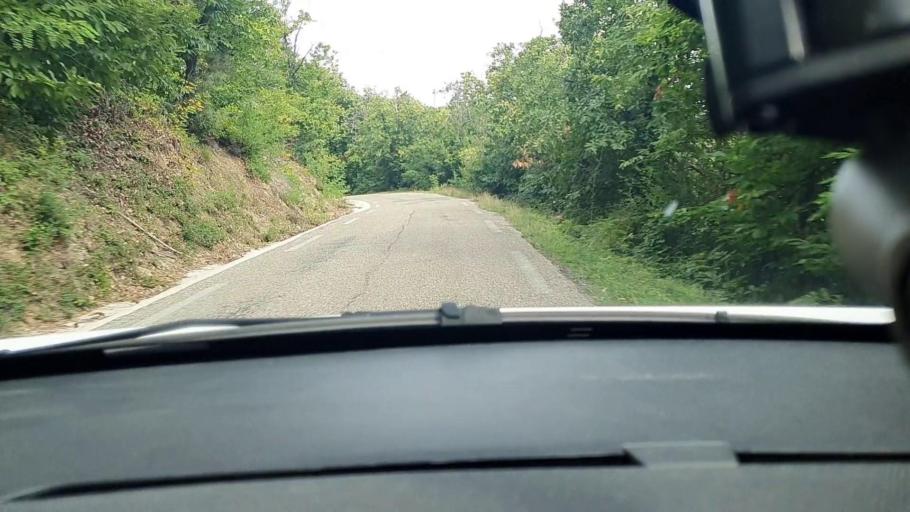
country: FR
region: Languedoc-Roussillon
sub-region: Departement du Gard
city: Branoux-les-Taillades
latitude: 44.2208
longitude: 3.9755
